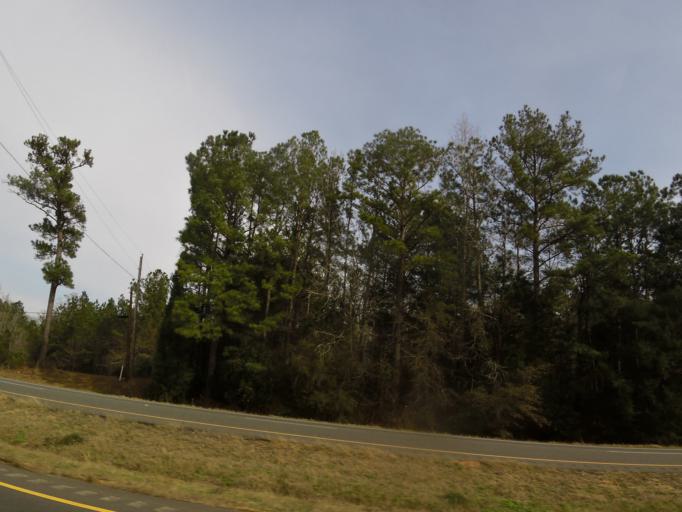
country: US
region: Alabama
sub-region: Dale County
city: Ozark
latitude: 31.4809
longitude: -85.6838
